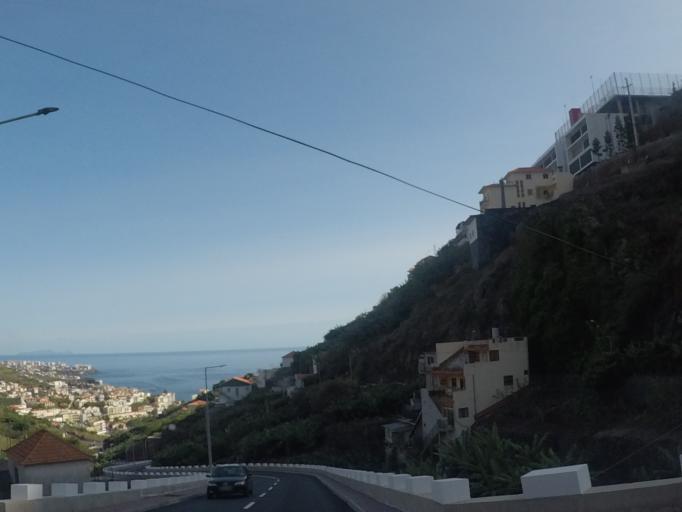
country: PT
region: Madeira
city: Camara de Lobos
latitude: 32.6567
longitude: -16.9907
